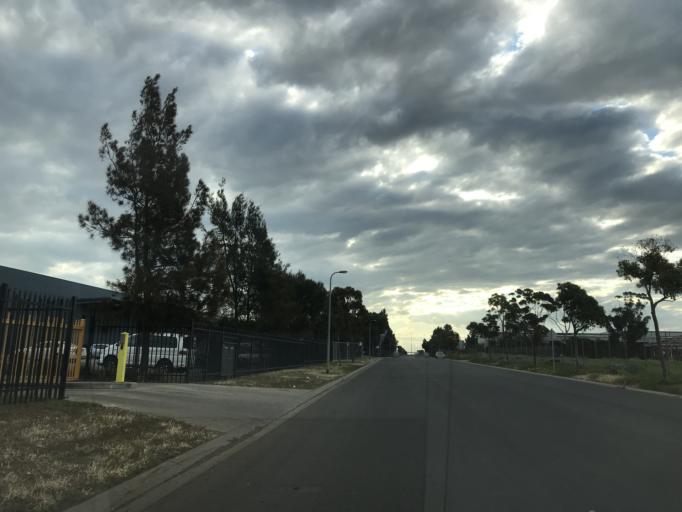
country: AU
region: Victoria
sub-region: Wyndham
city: Truganina
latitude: -37.8187
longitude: 144.7492
